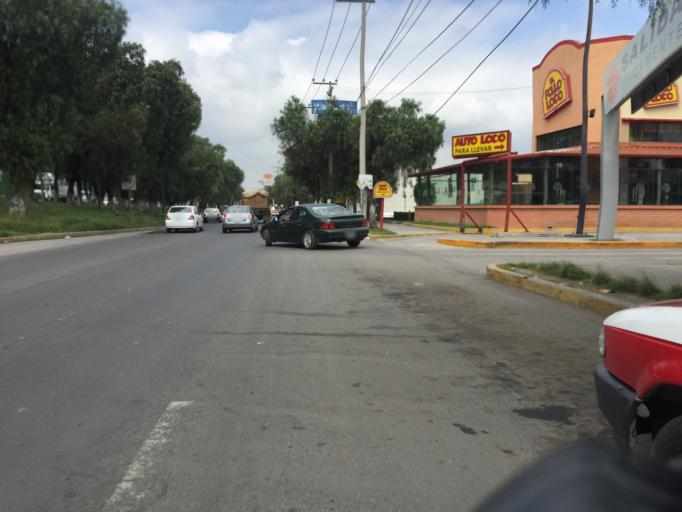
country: MX
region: Mexico
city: Cuautitlan
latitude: 19.6704
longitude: -99.2034
